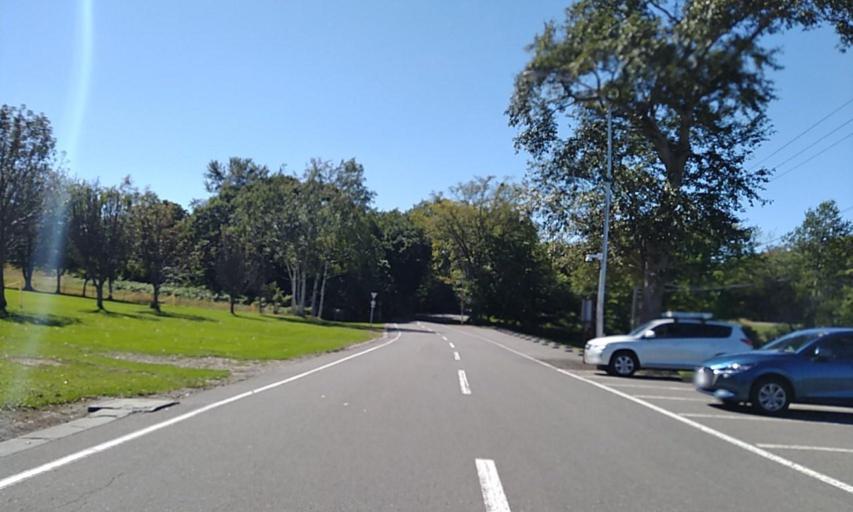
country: JP
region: Hokkaido
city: Sapporo
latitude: 42.9984
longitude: 141.3941
